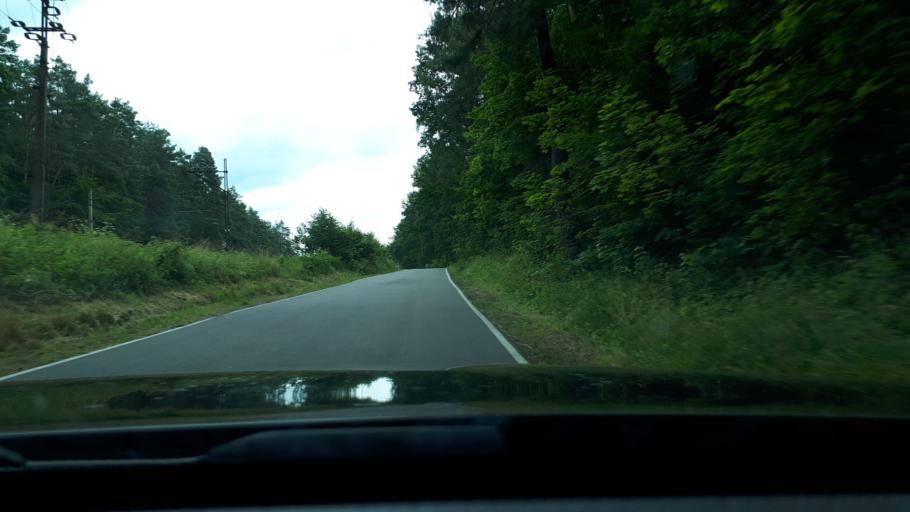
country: PL
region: Warmian-Masurian Voivodeship
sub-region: Powiat ostrodzki
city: Ostroda
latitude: 53.6901
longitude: 20.0849
